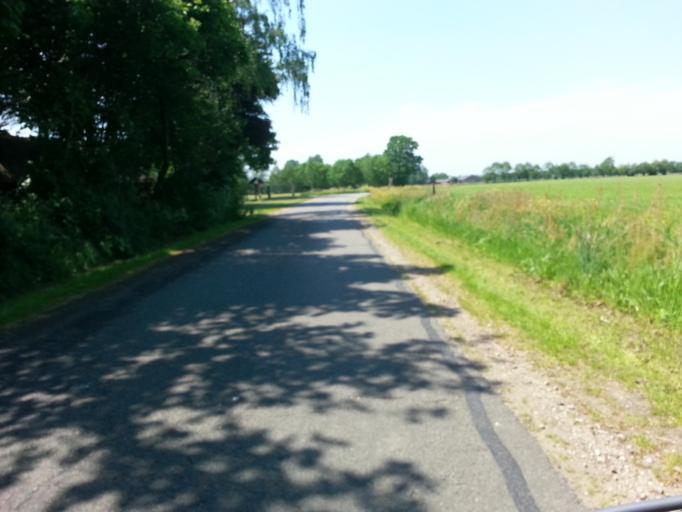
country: NL
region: Gelderland
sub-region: Gemeente Barneveld
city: Terschuur
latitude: 52.1415
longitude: 5.5111
